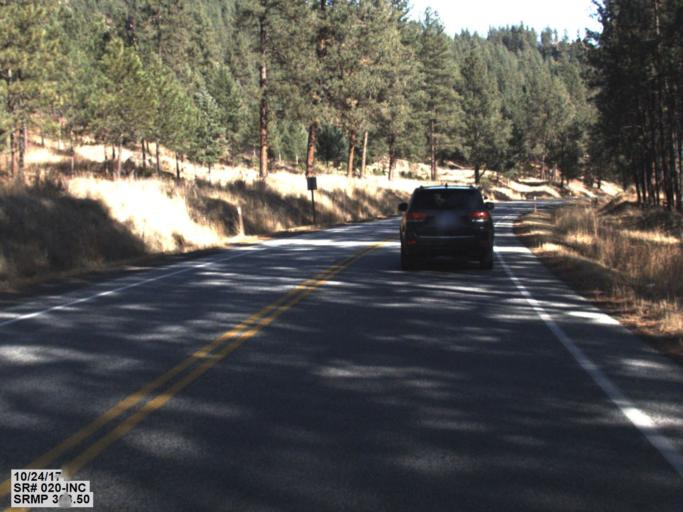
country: US
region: Washington
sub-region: Ferry County
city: Republic
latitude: 48.6478
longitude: -118.7197
